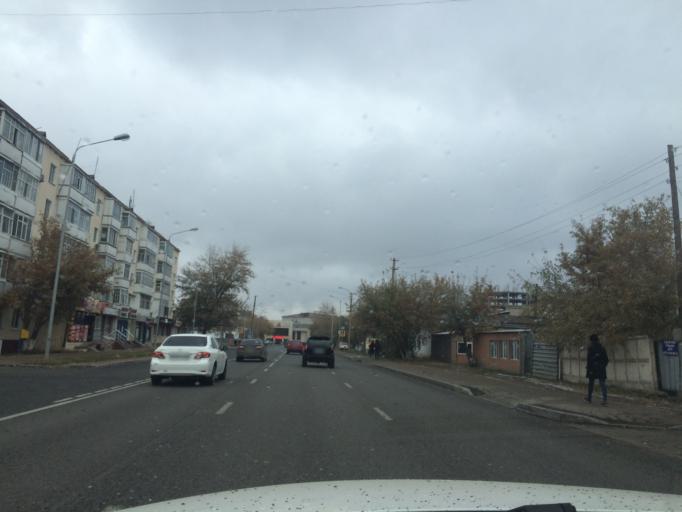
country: KZ
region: Astana Qalasy
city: Astana
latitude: 51.1705
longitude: 71.4449
